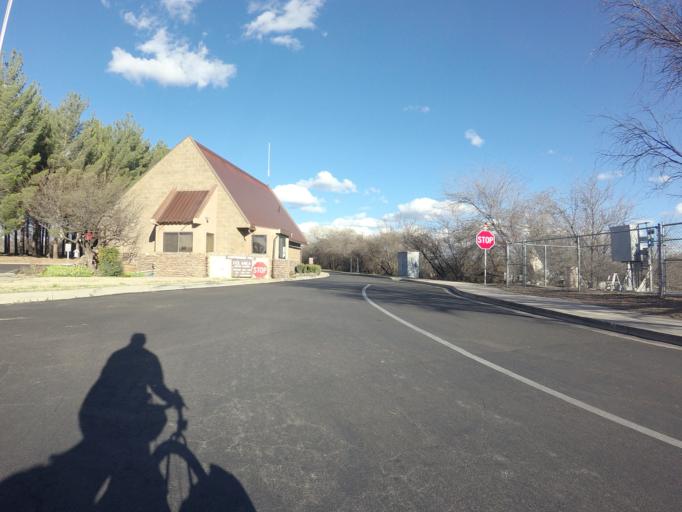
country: US
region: Arizona
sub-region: Yavapai County
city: Cottonwood
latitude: 34.7536
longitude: -112.0218
